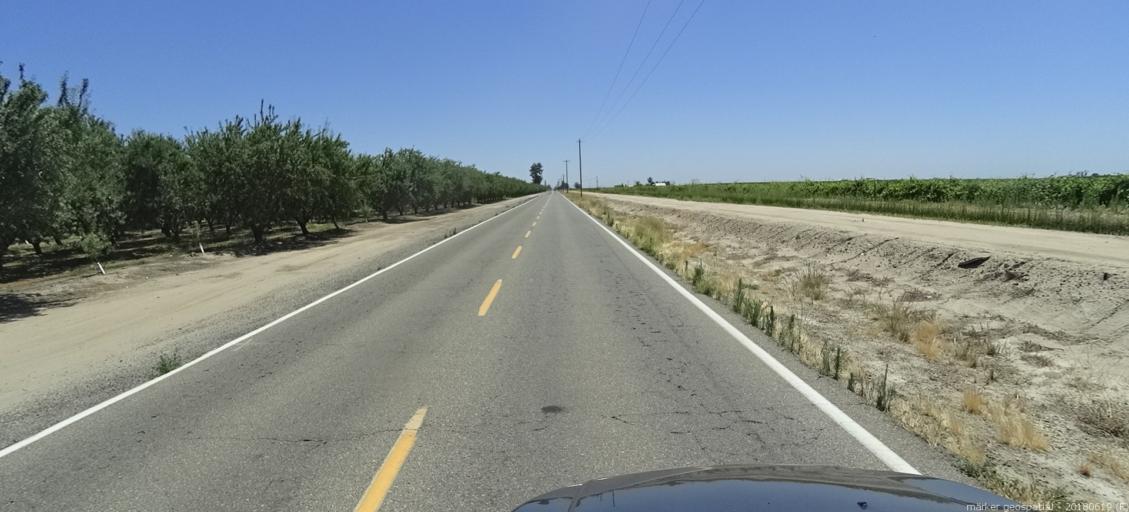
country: US
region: California
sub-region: Madera County
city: Parkwood
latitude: 36.8513
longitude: -120.1016
